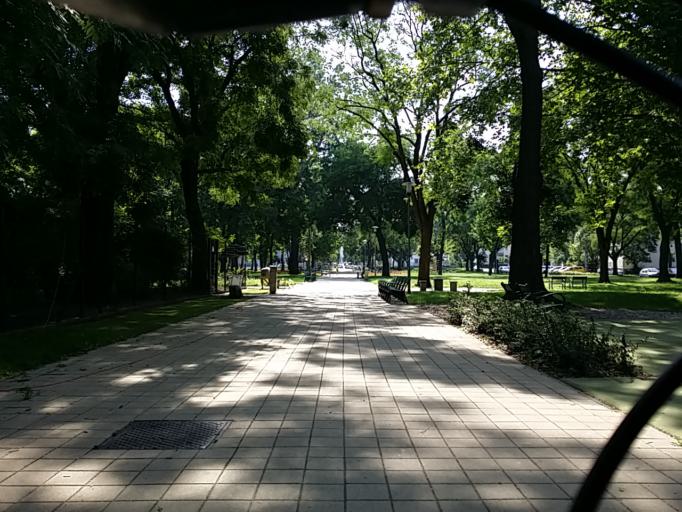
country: HU
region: Budapest
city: Budapest XIII. keruelet
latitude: 47.5446
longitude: 19.0857
